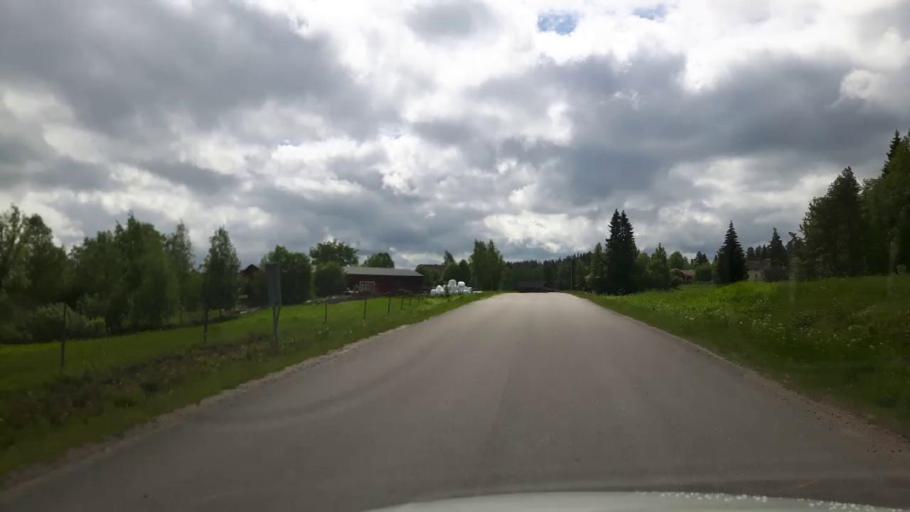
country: SE
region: Gaevleborg
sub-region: Ovanakers Kommun
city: Edsbyn
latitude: 61.3504
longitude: 15.9184
